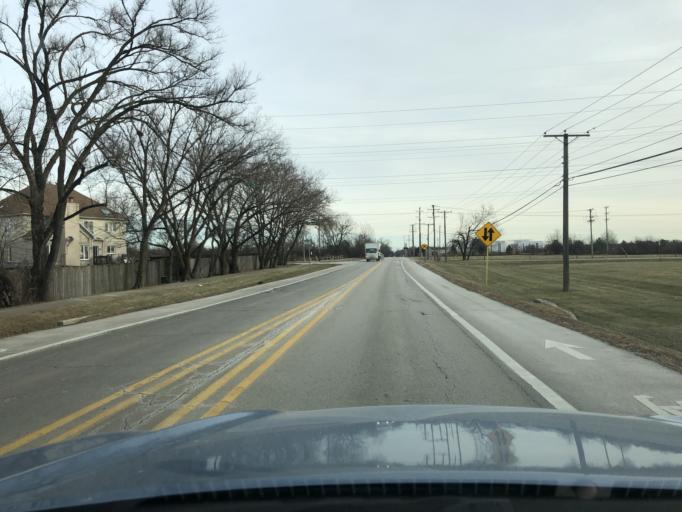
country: US
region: Illinois
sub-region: Cook County
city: Mount Prospect
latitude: 42.0661
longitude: -87.9033
